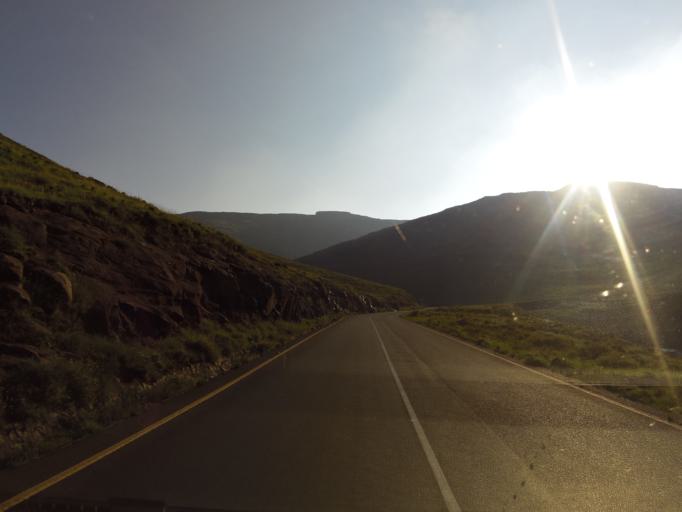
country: LS
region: Butha-Buthe
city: Butha-Buthe
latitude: -29.1183
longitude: 28.4428
